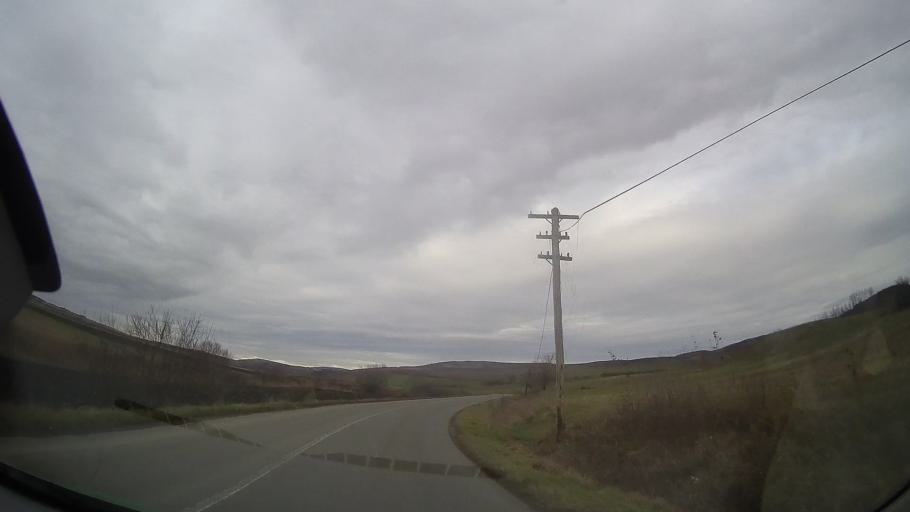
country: RO
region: Mures
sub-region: Comuna Faragau
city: Faragau
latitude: 46.7406
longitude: 24.5379
